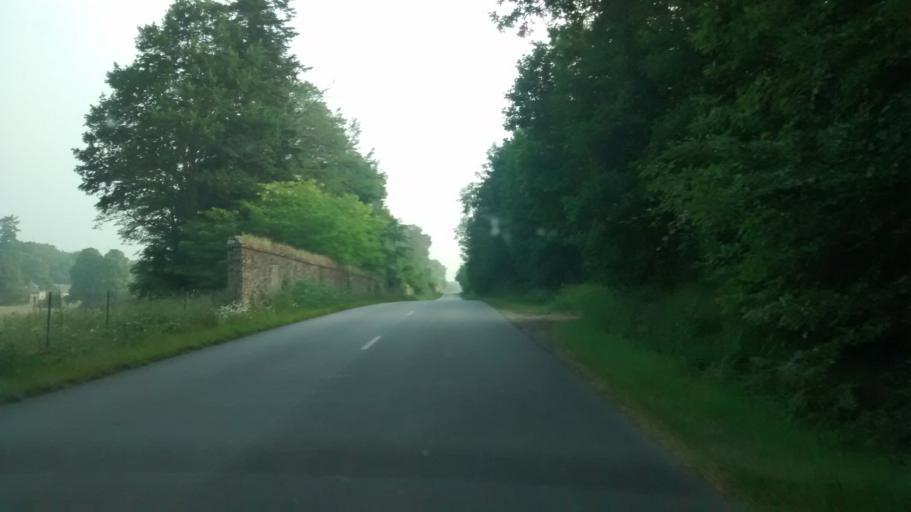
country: FR
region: Brittany
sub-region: Departement du Morbihan
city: Molac
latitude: 47.7623
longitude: -2.4360
